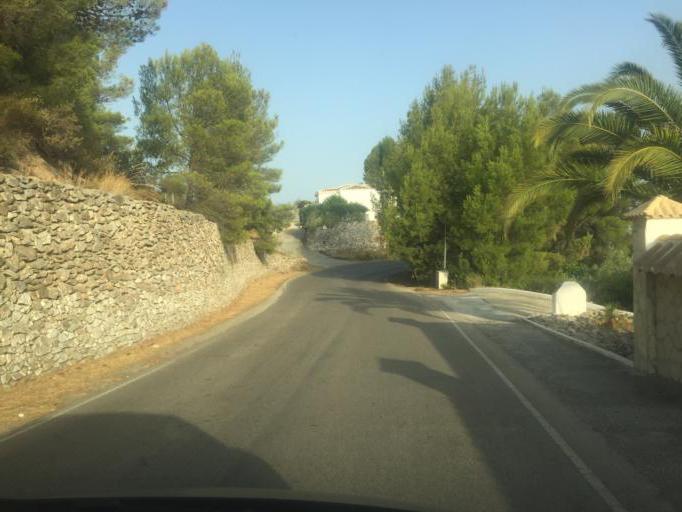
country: ES
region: Andalusia
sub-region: Provincia de Malaga
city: Frigiliana
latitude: 36.7985
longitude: -3.9052
